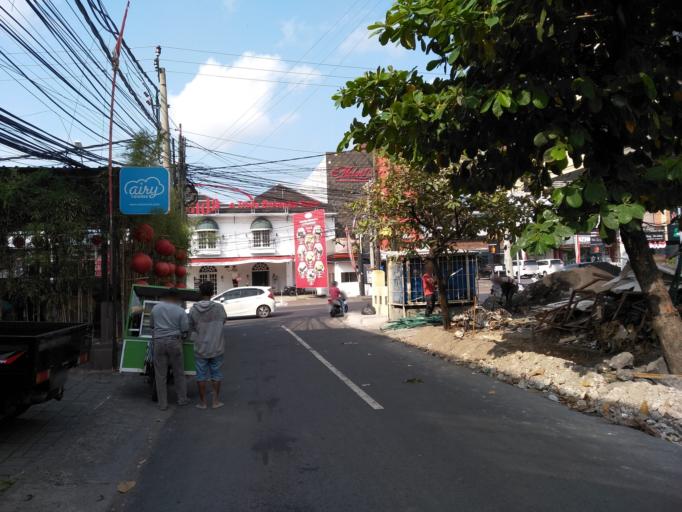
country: ID
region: Bali
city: Kuta
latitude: -8.7092
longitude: 115.1790
